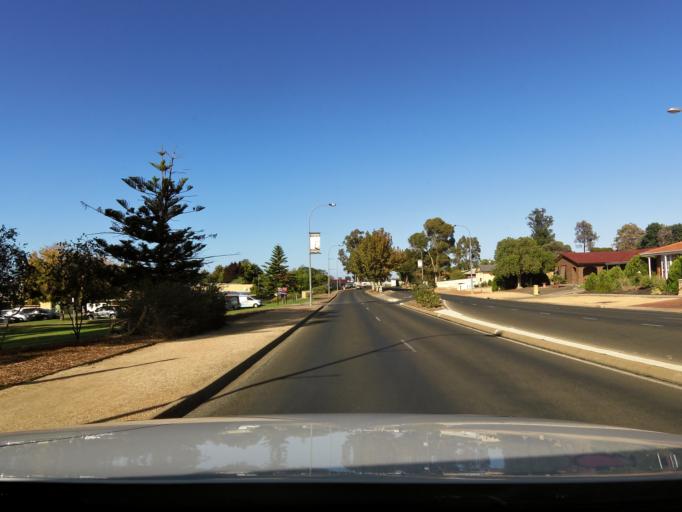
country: AU
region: South Australia
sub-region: Berri and Barmera
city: Berri
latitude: -34.2767
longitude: 140.6103
